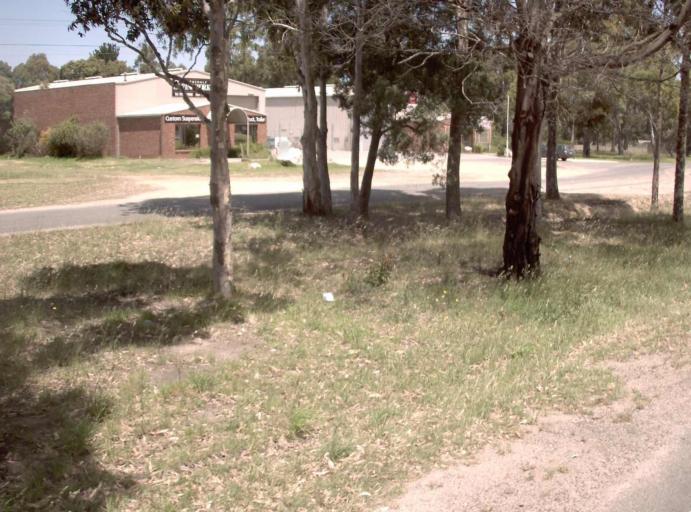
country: AU
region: Victoria
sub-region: East Gippsland
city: Bairnsdale
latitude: -37.8411
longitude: 147.5926
